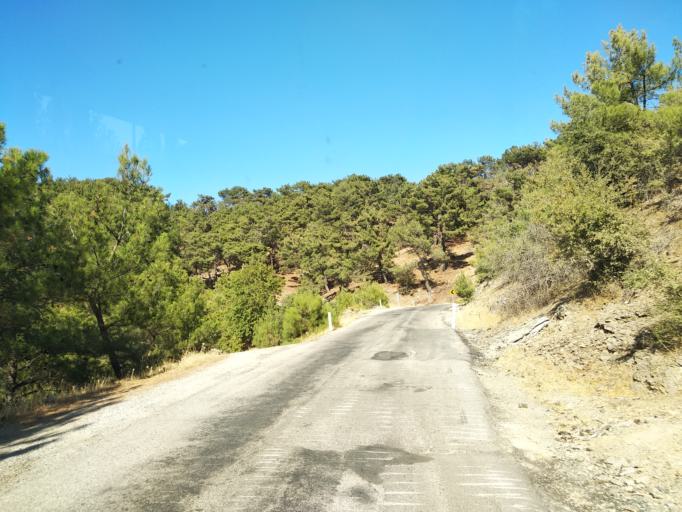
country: TR
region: Izmir
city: Gaziemir
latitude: 38.3004
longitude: 26.9978
